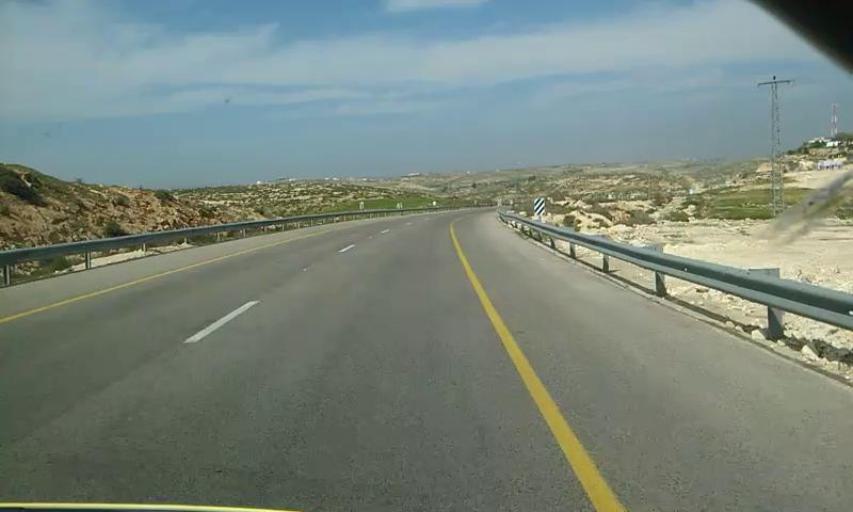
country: PS
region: West Bank
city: Az Zahiriyah
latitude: 31.3835
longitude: 35.0054
